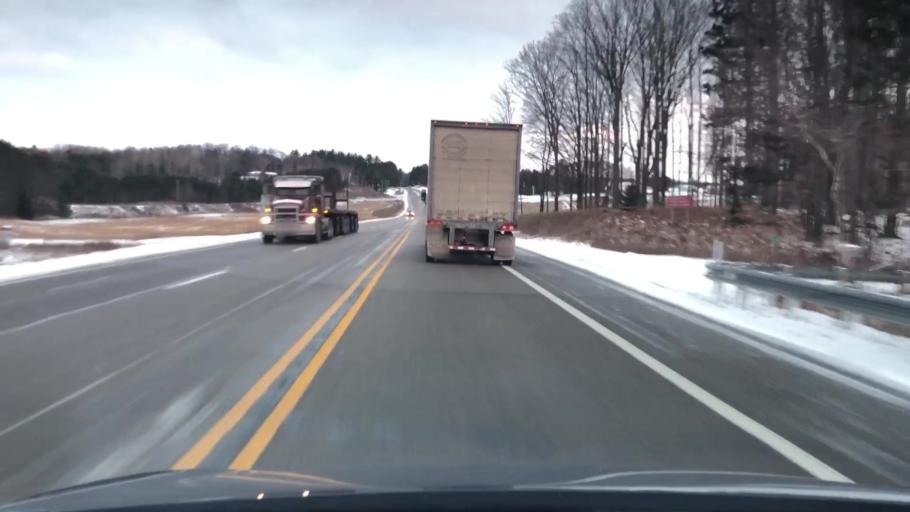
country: US
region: Michigan
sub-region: Wexford County
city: Cadillac
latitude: 44.1900
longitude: -85.3917
